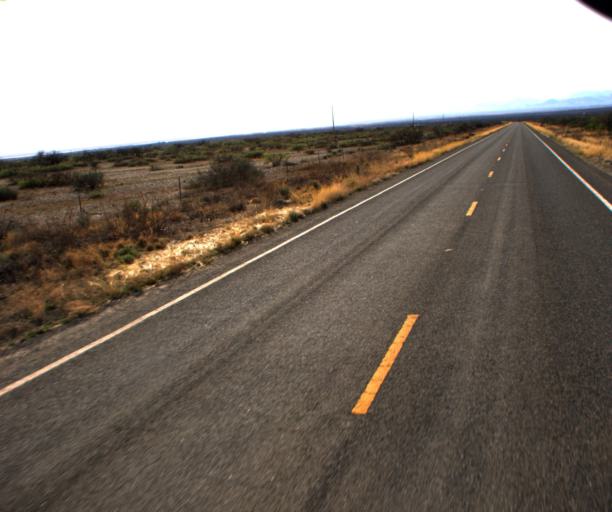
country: US
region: Arizona
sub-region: Cochise County
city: Willcox
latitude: 32.1932
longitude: -109.7020
